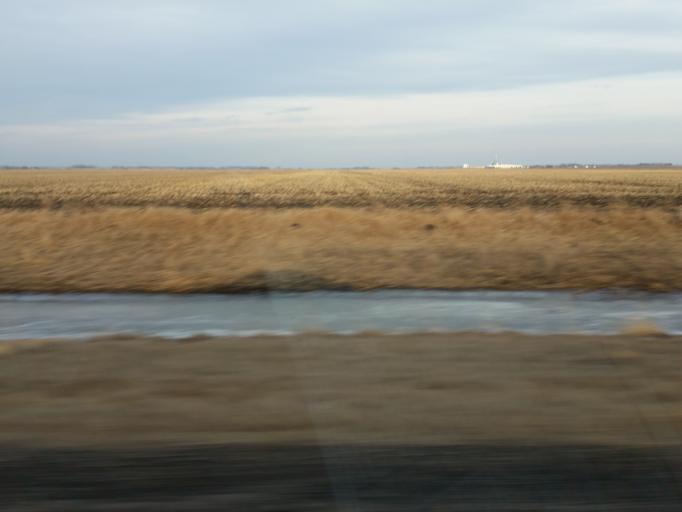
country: US
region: North Dakota
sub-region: Traill County
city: Hillsboro
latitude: 47.3268
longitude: -97.2177
